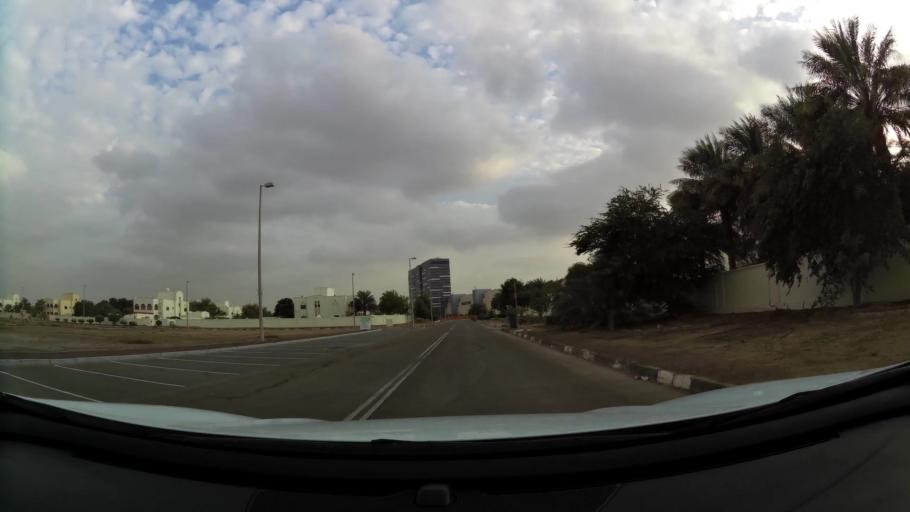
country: AE
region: Abu Dhabi
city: Abu Dhabi
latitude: 24.3809
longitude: 54.5308
